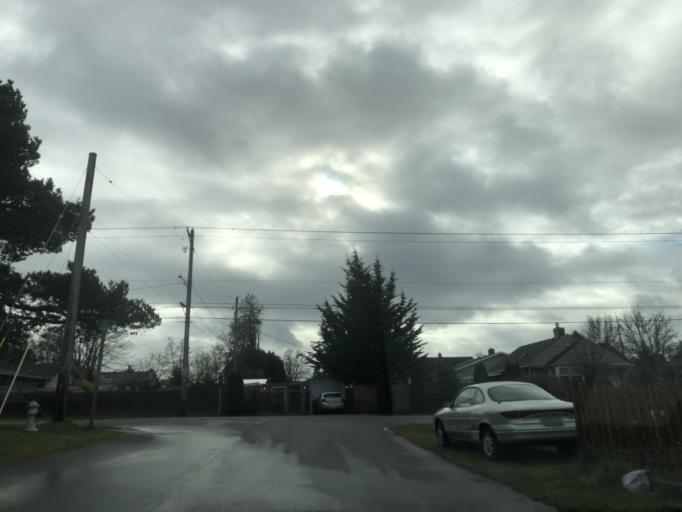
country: US
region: Washington
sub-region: Pierce County
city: Tacoma
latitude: 47.2284
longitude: -122.4530
